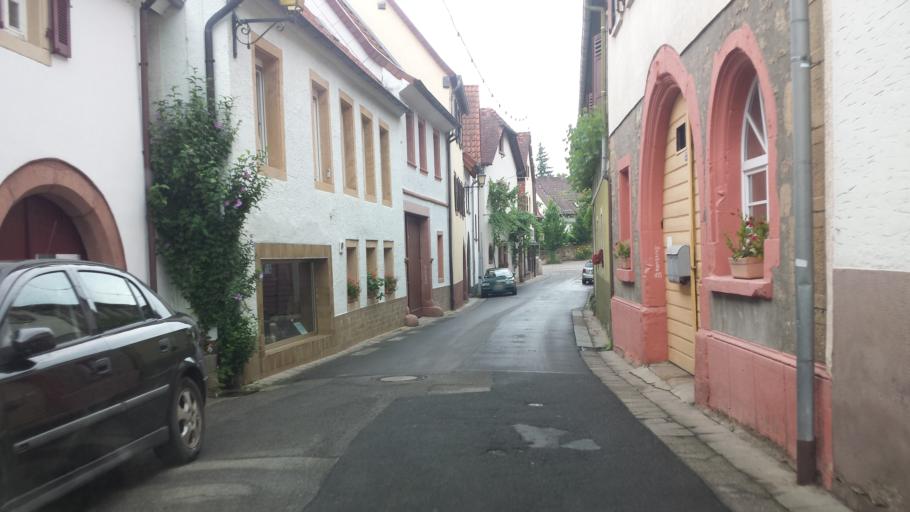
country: DE
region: Rheinland-Pfalz
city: Neustadt
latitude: 49.3300
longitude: 8.1299
